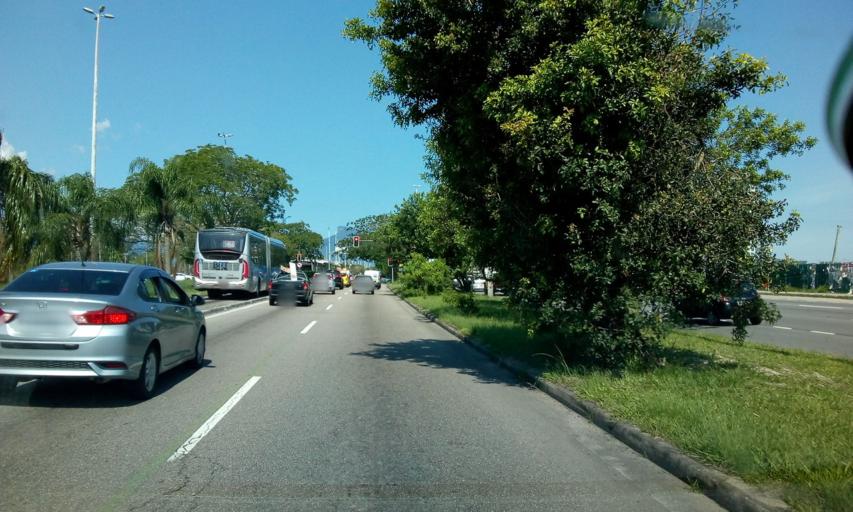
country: BR
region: Rio de Janeiro
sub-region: Nilopolis
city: Nilopolis
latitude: -23.0000
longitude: -43.4091
